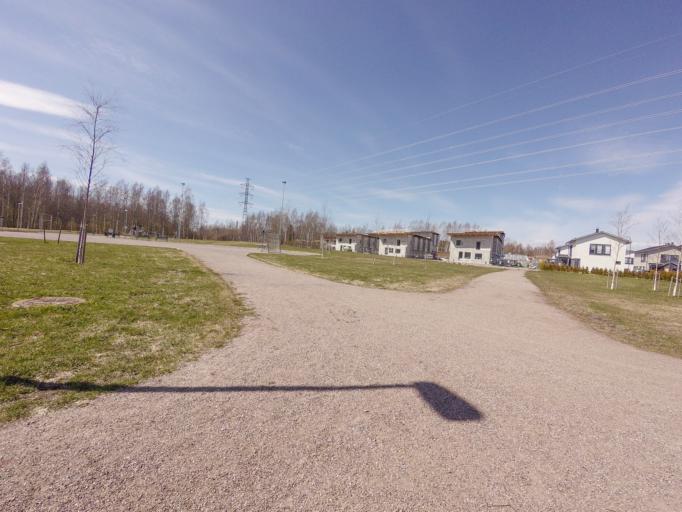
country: FI
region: Uusimaa
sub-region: Helsinki
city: Vantaa
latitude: 60.2302
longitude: 25.1077
